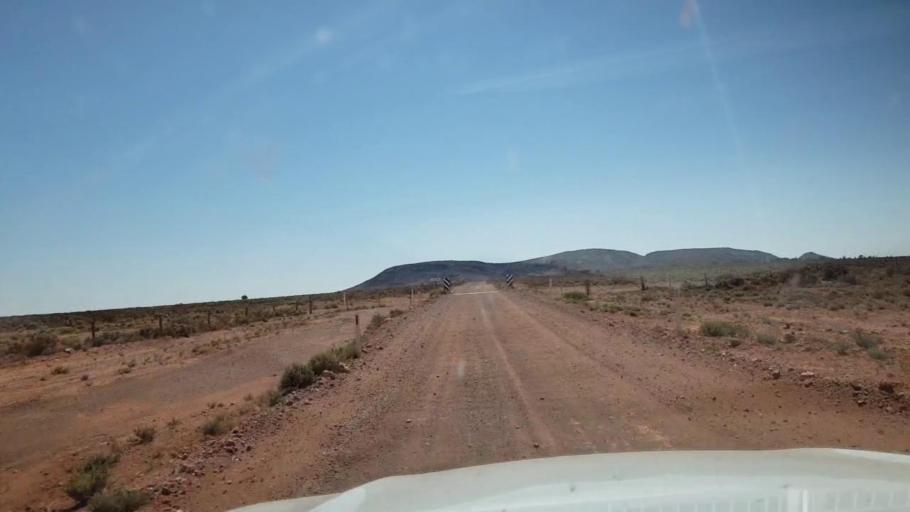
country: AU
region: South Australia
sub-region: Whyalla
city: Whyalla
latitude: -32.7089
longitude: 137.1391
